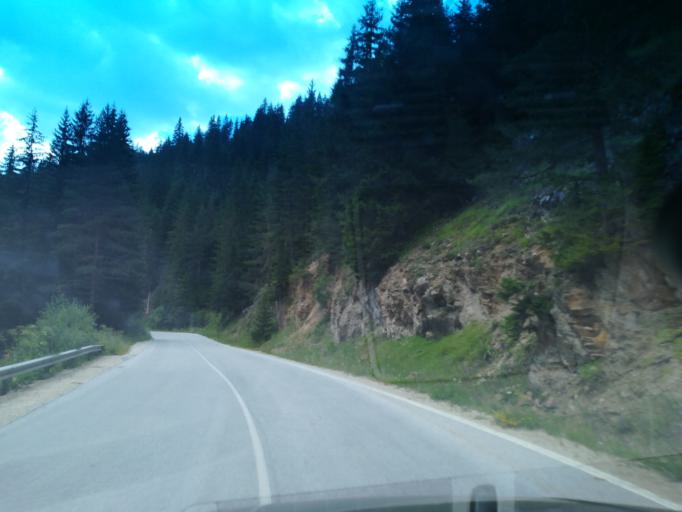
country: BG
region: Smolyan
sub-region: Obshtina Chepelare
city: Chepelare
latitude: 41.6635
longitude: 24.6601
